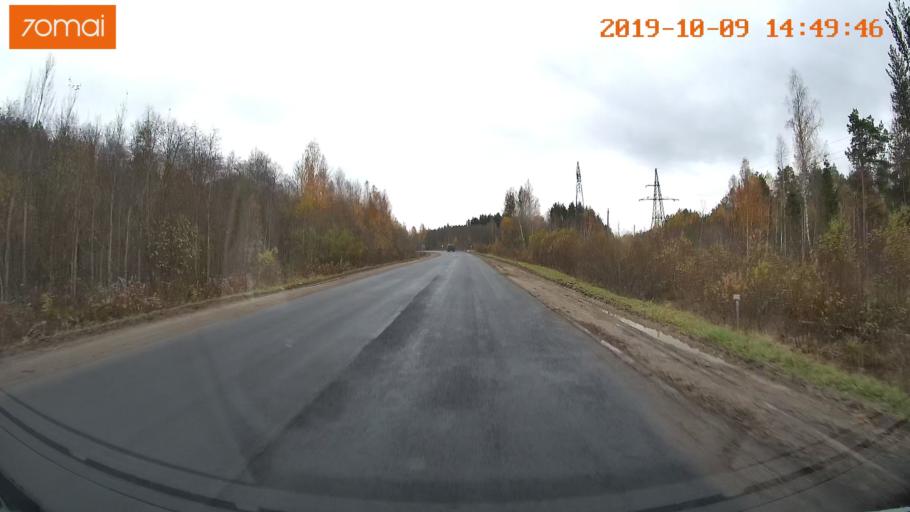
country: RU
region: Kostroma
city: Chistyye Bory
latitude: 58.3901
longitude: 41.5874
